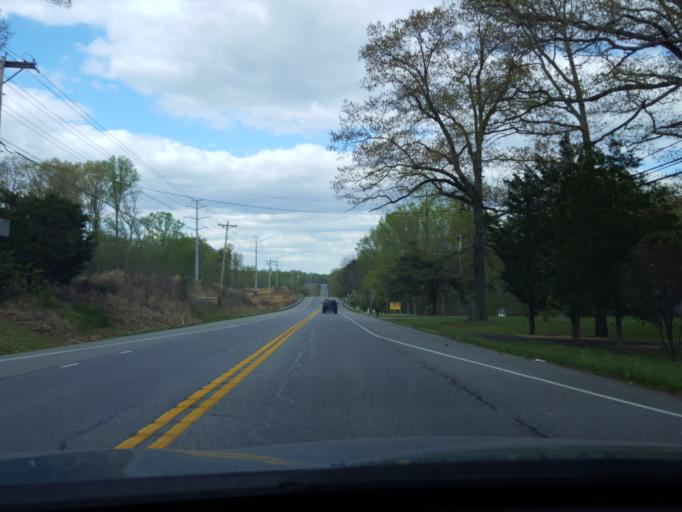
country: US
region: Maryland
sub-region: Charles County
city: La Plata
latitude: 38.5408
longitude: -76.9377
